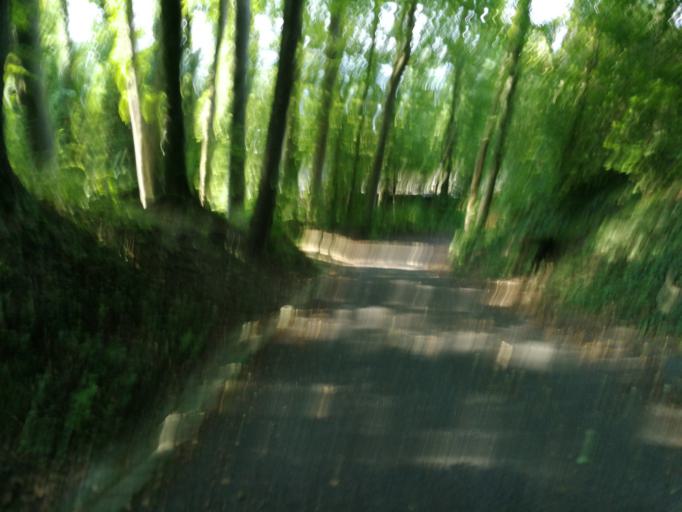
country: CH
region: Zurich
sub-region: Bezirk Meilen
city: Uetikon
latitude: 47.2685
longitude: 8.6867
